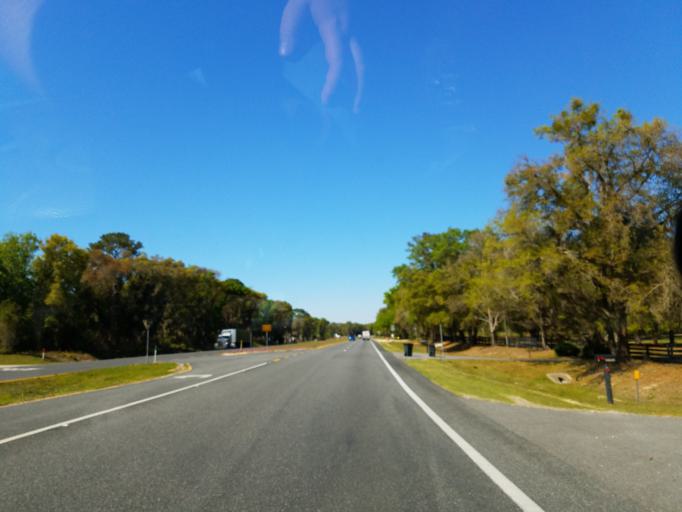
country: US
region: Florida
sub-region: Marion County
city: Belleview
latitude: 29.0149
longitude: -82.0440
